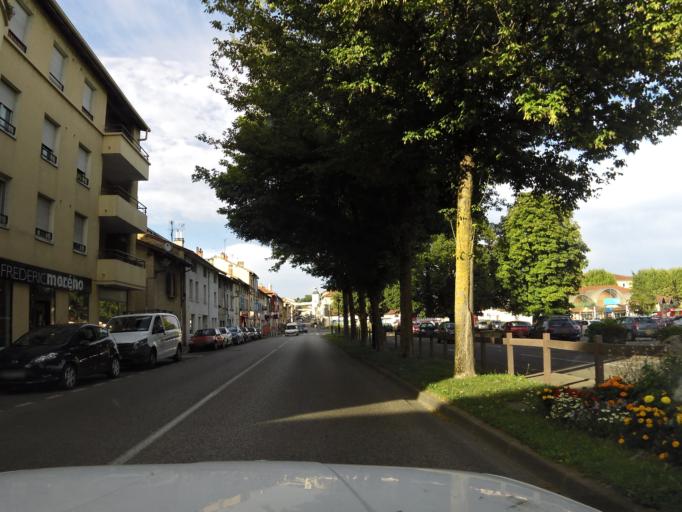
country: FR
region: Rhone-Alpes
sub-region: Departement de l'Ain
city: Meximieux
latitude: 45.9008
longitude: 5.1888
